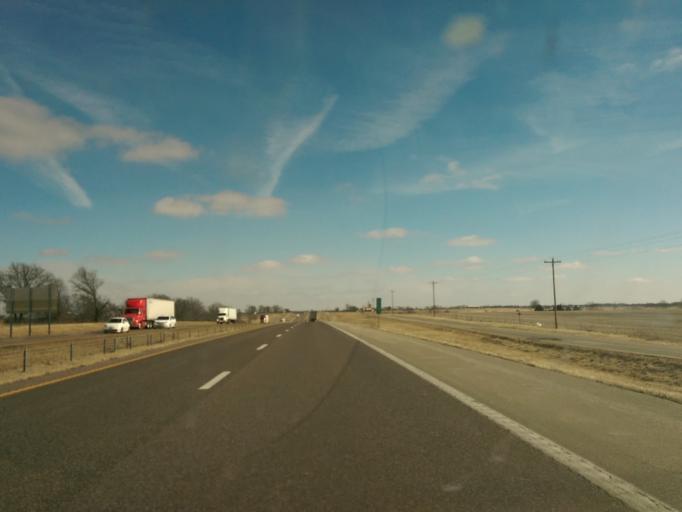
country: US
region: Missouri
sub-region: Callaway County
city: Fulton
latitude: 38.9440
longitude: -91.9170
